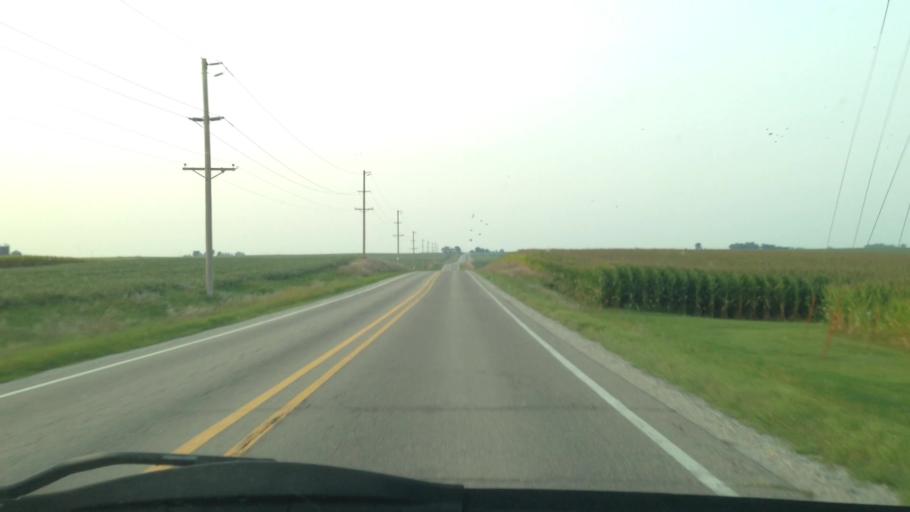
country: US
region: Iowa
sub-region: Iowa County
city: Marengo
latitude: 41.9428
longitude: -92.0850
